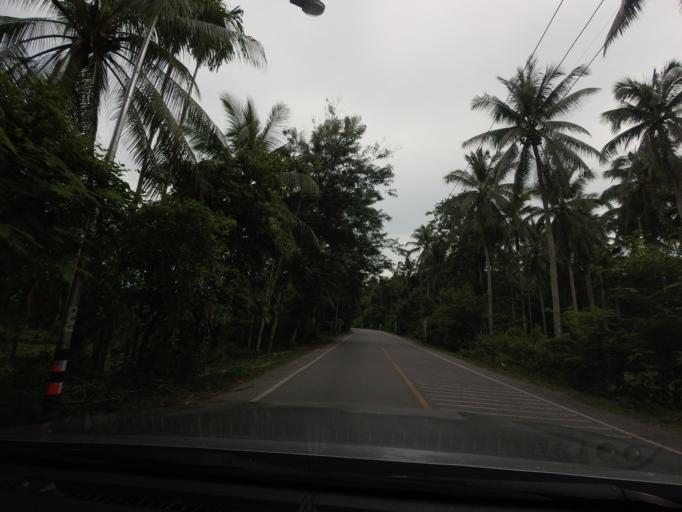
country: TH
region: Yala
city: Raman
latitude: 6.4375
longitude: 101.4550
